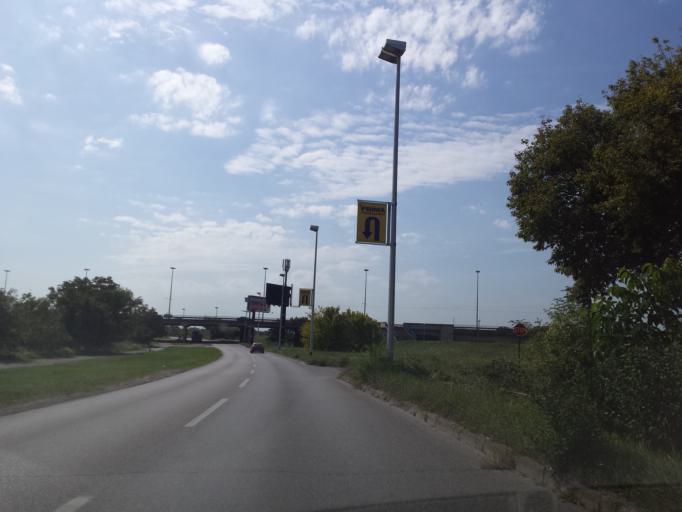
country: HR
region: Grad Zagreb
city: Novi Zagreb
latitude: 45.7823
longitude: 15.9545
